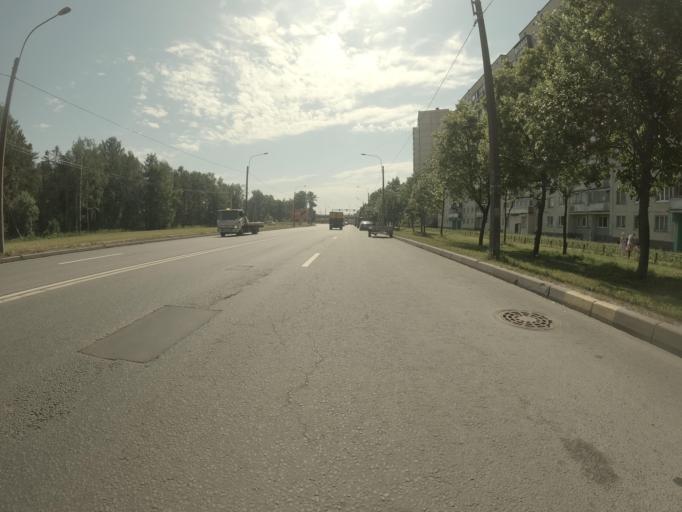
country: RU
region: St.-Petersburg
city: Krasnogvargeisky
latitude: 59.9479
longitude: 30.5032
